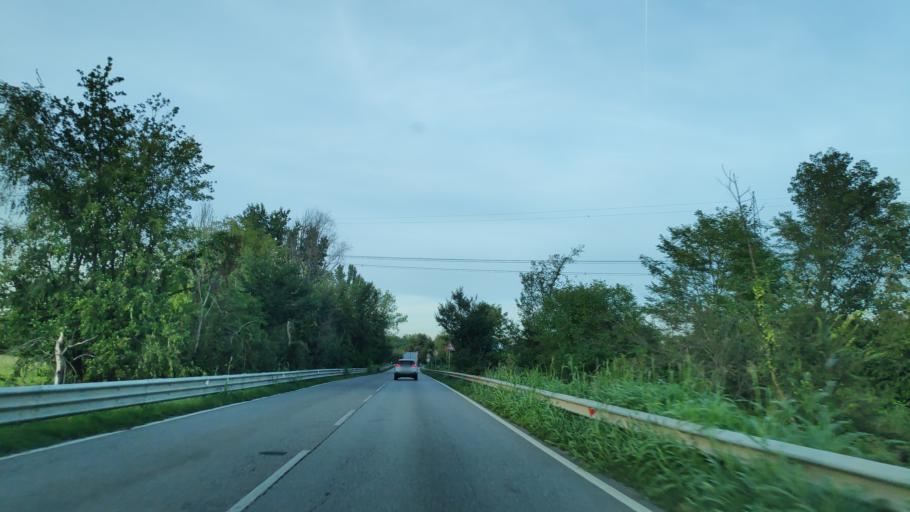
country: IT
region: Lombardy
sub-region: Citta metropolitana di Milano
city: Liscate
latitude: 45.4637
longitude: 9.4056
